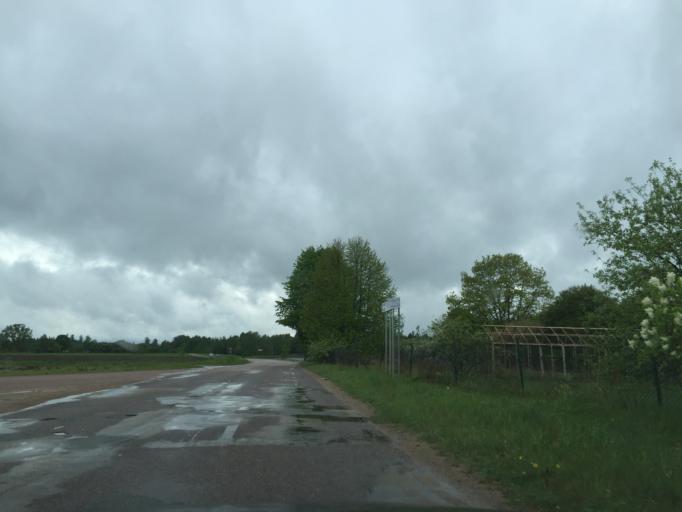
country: LV
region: Ogre
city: Jumprava
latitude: 56.6718
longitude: 24.9653
